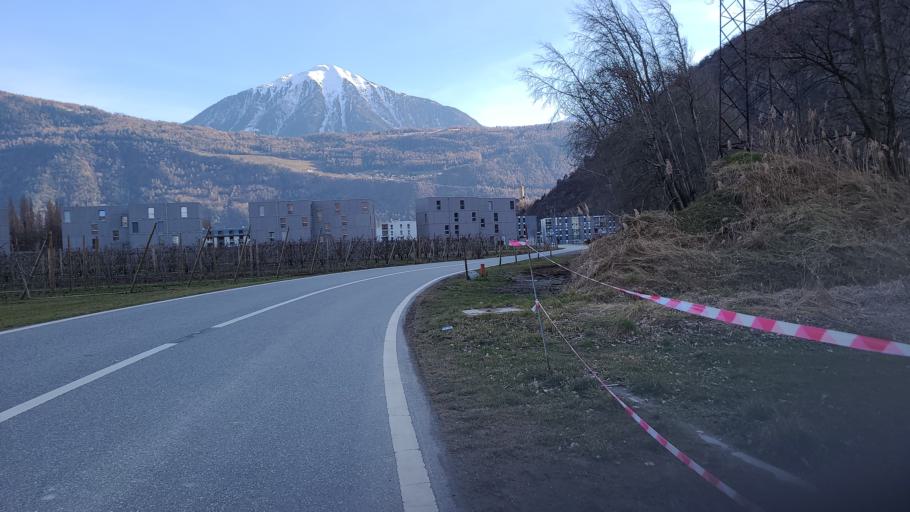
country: CH
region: Valais
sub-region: Martigny District
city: Martigny-Ville
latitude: 46.1159
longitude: 7.0662
